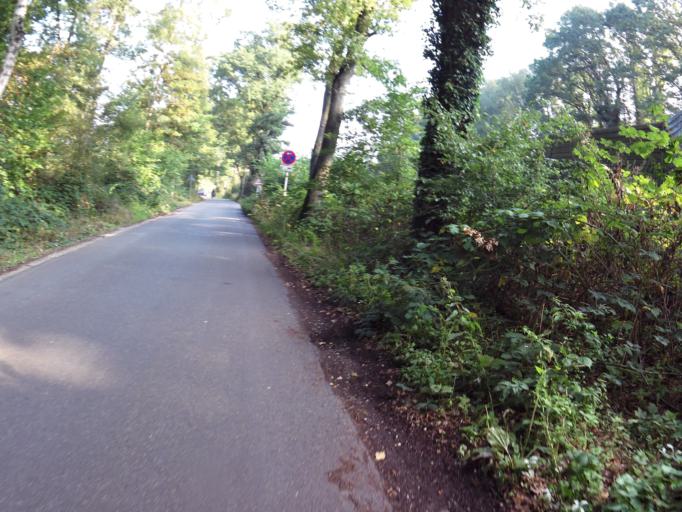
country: DE
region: Lower Saxony
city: Verden
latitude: 52.9442
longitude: 9.2309
